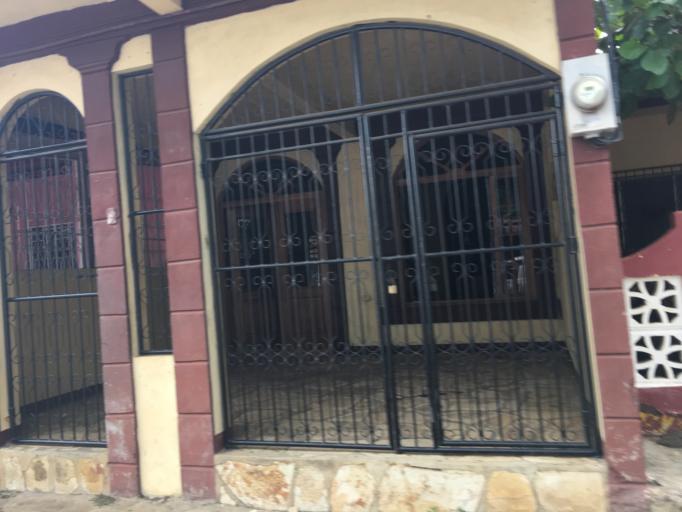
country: NI
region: Masaya
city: Masaya
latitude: 11.9831
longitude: -86.0942
